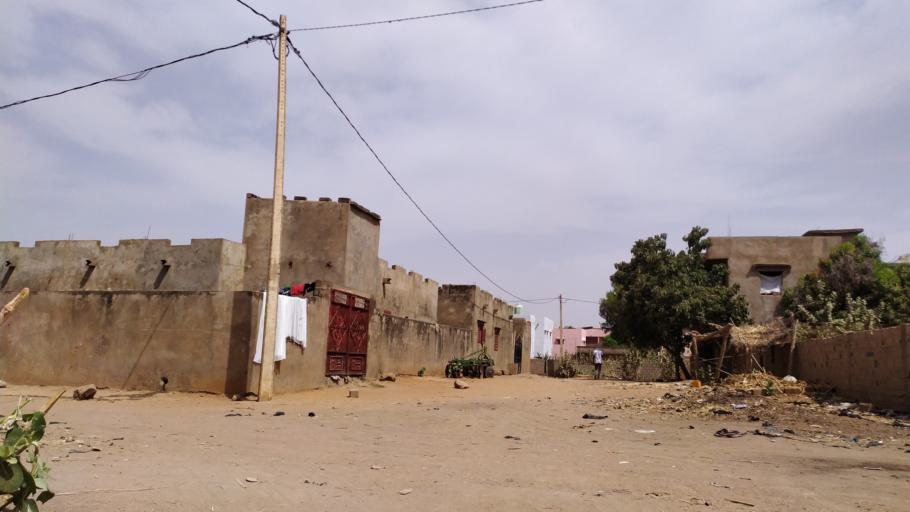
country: ML
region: Kayes
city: Kayes
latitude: 14.4555
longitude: -11.4649
